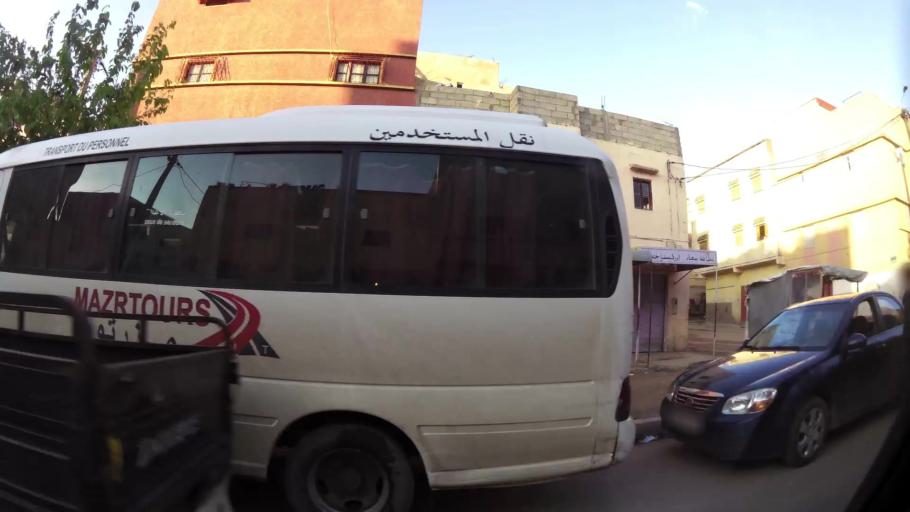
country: MA
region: Chaouia-Ouardigha
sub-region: Settat Province
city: Settat
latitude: 32.9962
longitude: -7.6061
